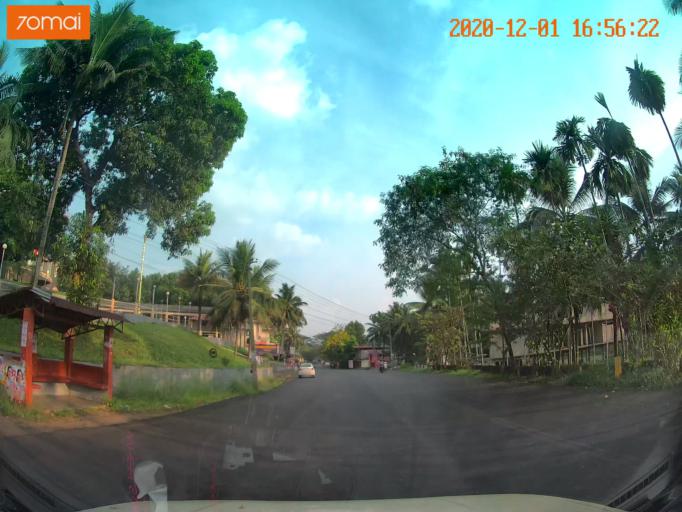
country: IN
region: Kerala
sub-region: Ernakulam
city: Muvattupula
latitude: 9.9640
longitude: 76.6160
